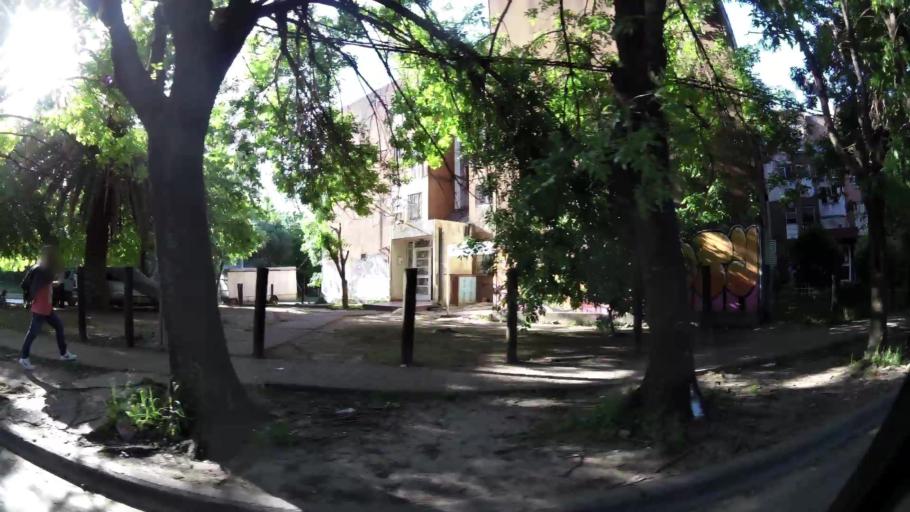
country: AR
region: Buenos Aires
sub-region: Partido de Almirante Brown
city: Adrogue
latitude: -34.8116
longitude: -58.3330
